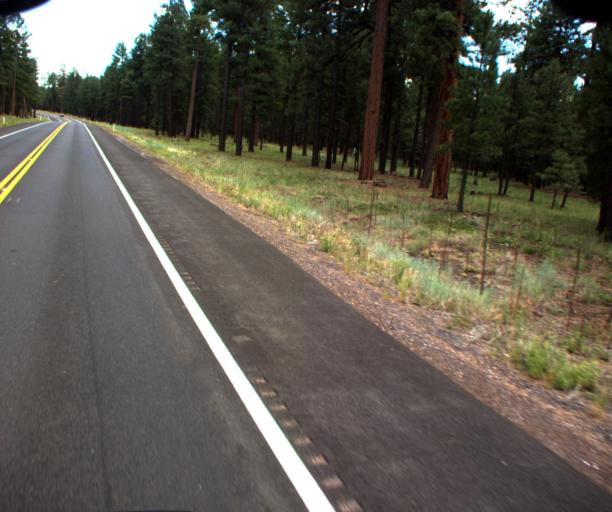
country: US
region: Arizona
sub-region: Coconino County
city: Flagstaff
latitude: 35.2537
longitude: -111.7000
